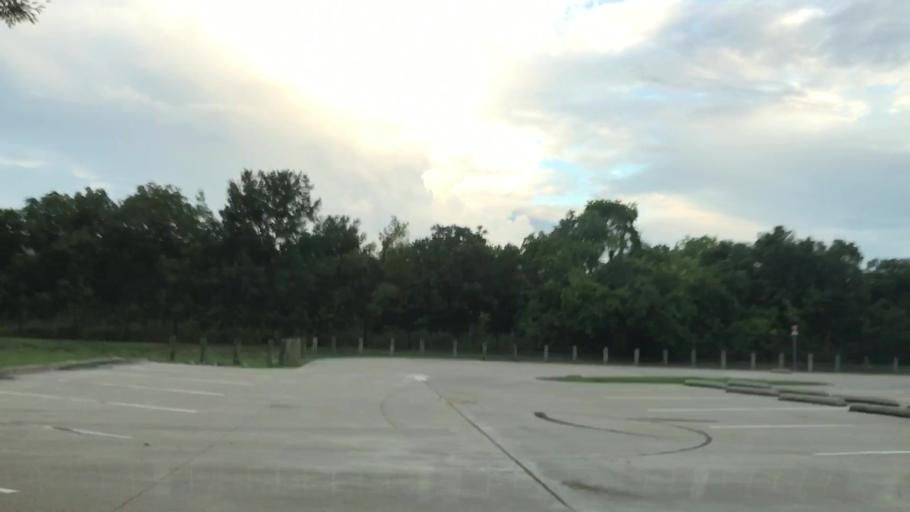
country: US
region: Texas
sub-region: Dallas County
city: Addison
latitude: 33.0103
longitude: -96.8198
